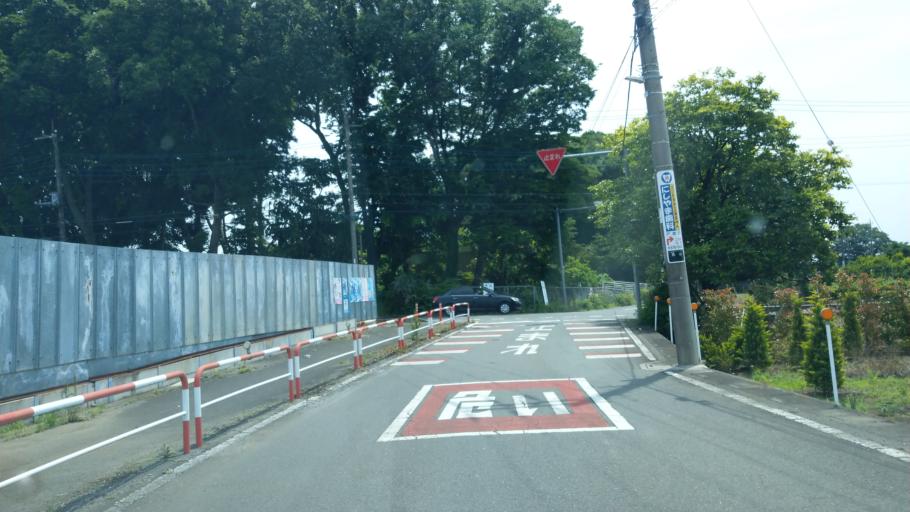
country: JP
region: Saitama
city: Saitama
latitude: 35.8984
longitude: 139.6788
